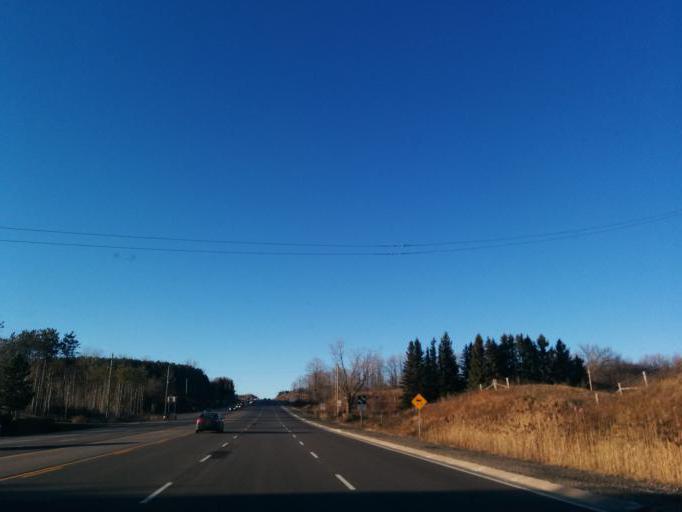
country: CA
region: Ontario
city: Orangeville
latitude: 43.8327
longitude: -79.9584
